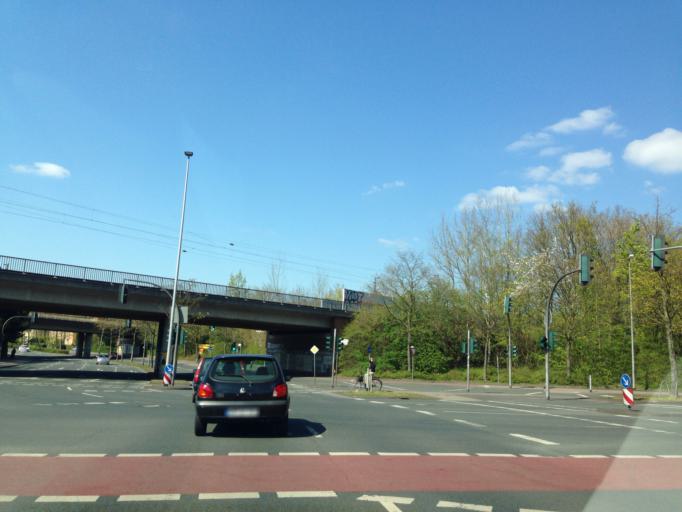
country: DE
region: North Rhine-Westphalia
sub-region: Regierungsbezirk Munster
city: Muenster
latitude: 51.9674
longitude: 7.6457
